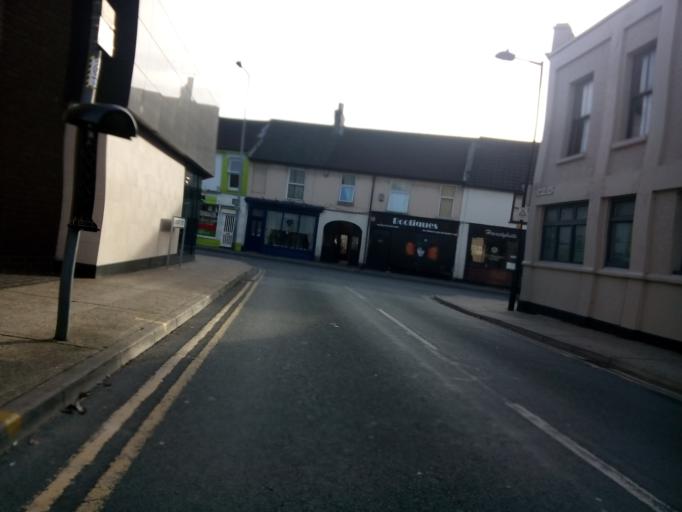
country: GB
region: England
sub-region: Suffolk
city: Ipswich
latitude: 52.0611
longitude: 1.1452
